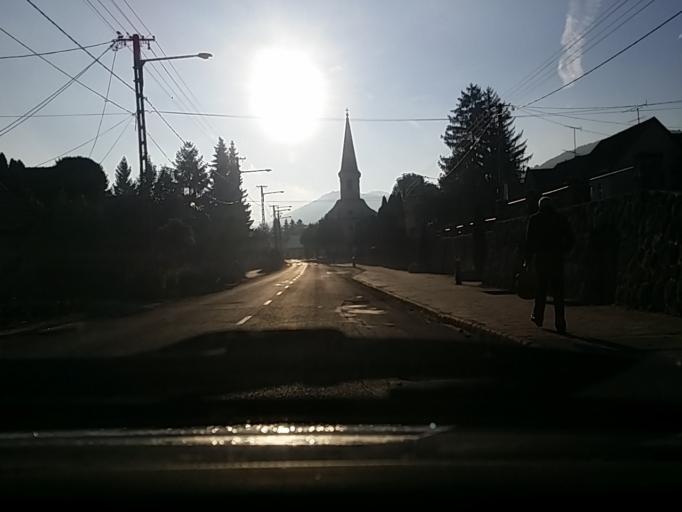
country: HU
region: Komarom-Esztergom
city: Pilismarot
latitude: 47.7642
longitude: 18.9094
